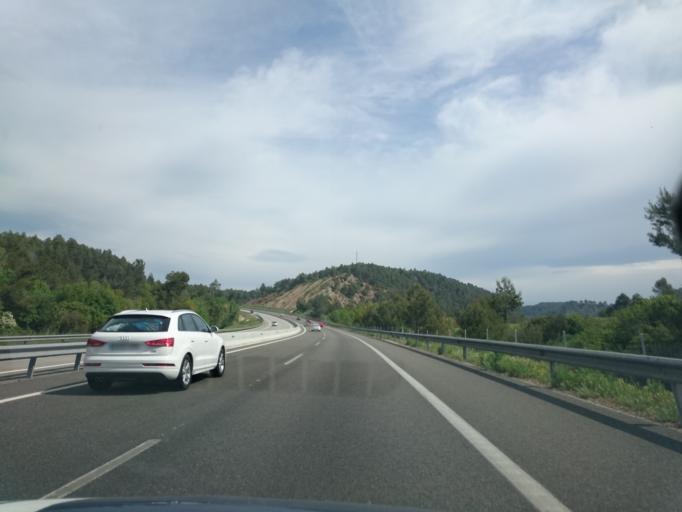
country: ES
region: Catalonia
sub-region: Provincia de Barcelona
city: Avinyo
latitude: 41.8396
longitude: 1.9814
